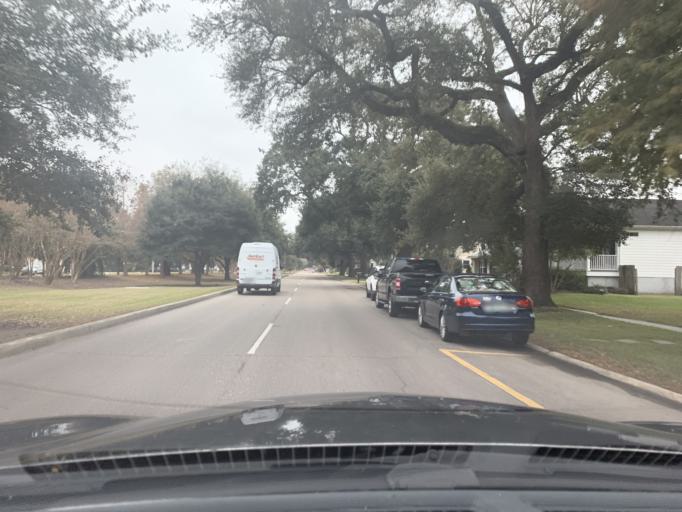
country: US
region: Louisiana
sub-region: Jefferson Parish
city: Metairie
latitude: 30.0152
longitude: -90.1070
